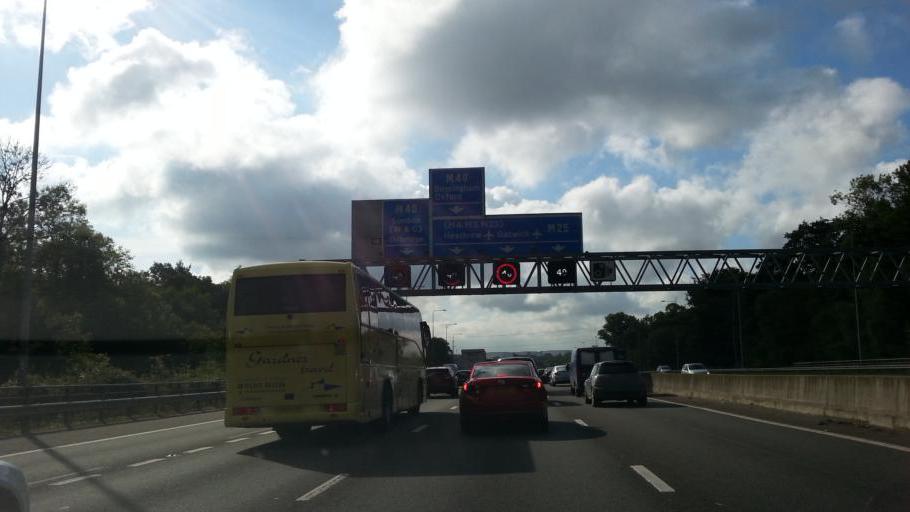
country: GB
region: England
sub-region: Buckinghamshire
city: Gerrards Cross
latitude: 51.5701
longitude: -0.5348
